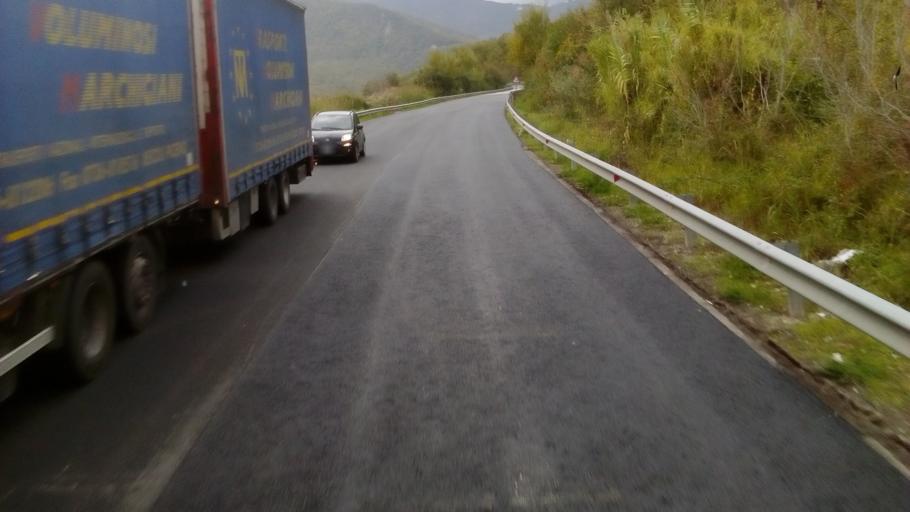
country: IT
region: Abruzzo
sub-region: Provincia di Chieti
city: Dogliola
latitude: 41.9277
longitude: 14.6642
